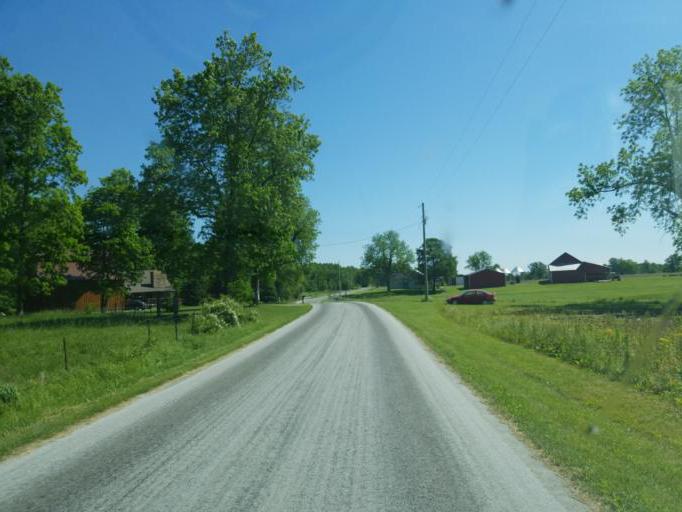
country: US
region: Ohio
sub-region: Hardin County
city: Kenton
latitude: 40.6068
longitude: -83.5134
